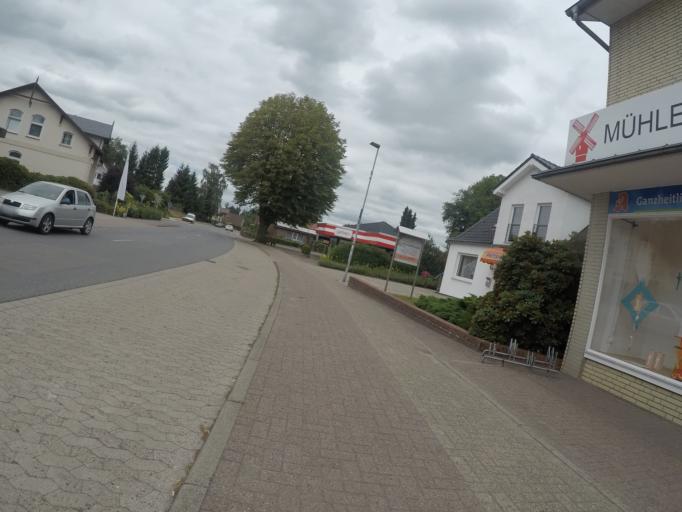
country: DE
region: Lower Saxony
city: Himmelpforten
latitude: 53.6156
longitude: 9.3062
